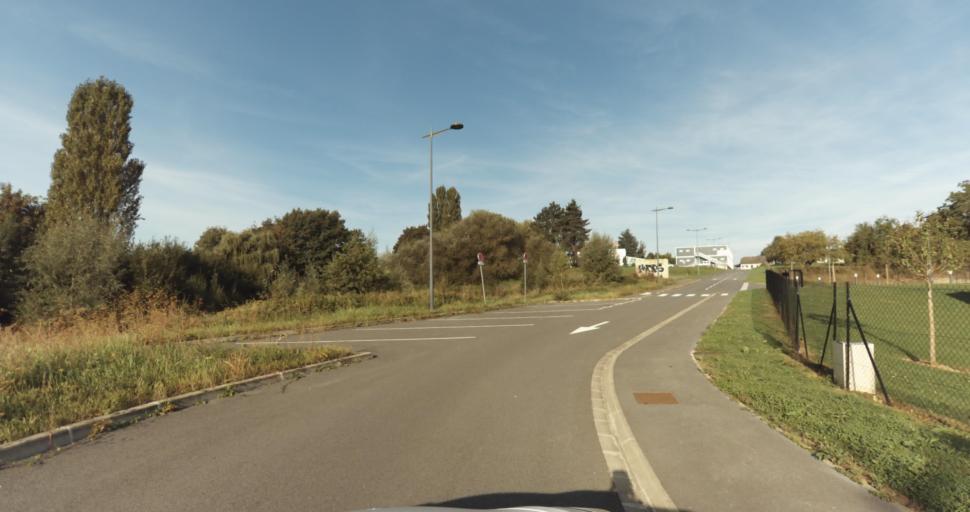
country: FR
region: Champagne-Ardenne
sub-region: Departement des Ardennes
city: Villers-Semeuse
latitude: 49.7361
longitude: 4.7473
